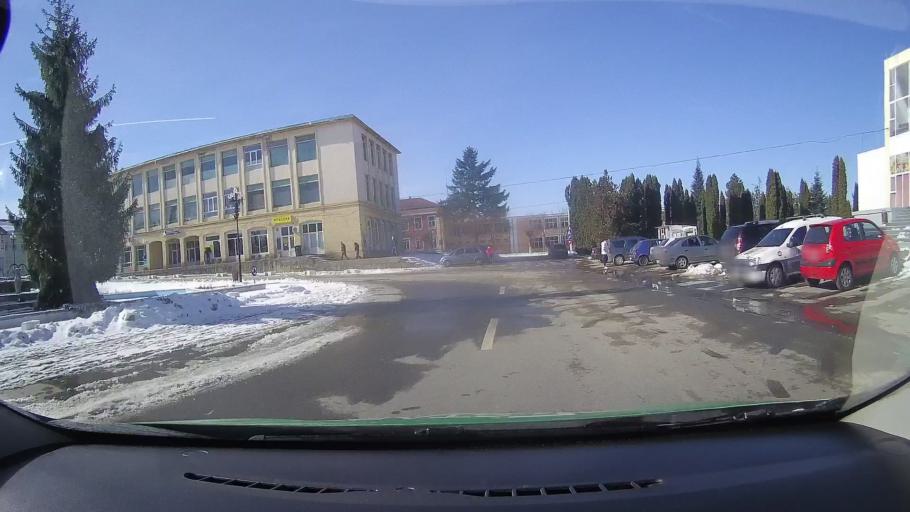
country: RO
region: Brasov
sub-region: Oras Victoria
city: Victoria
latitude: 45.7301
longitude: 24.7013
